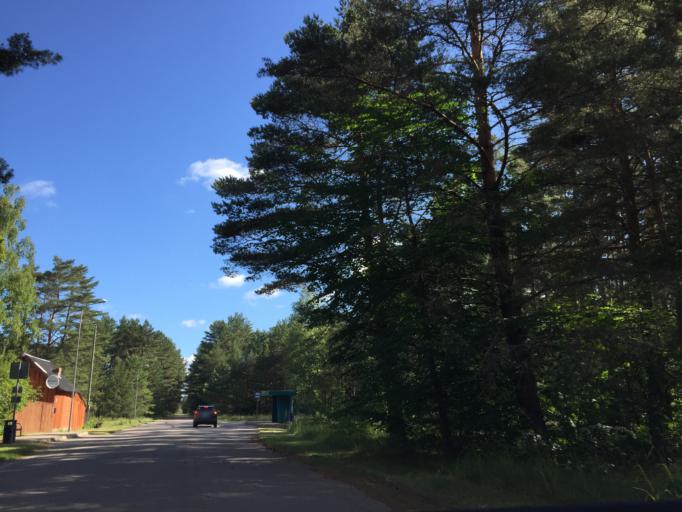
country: LV
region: Ventspils
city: Ventspils
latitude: 57.4469
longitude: 21.6234
